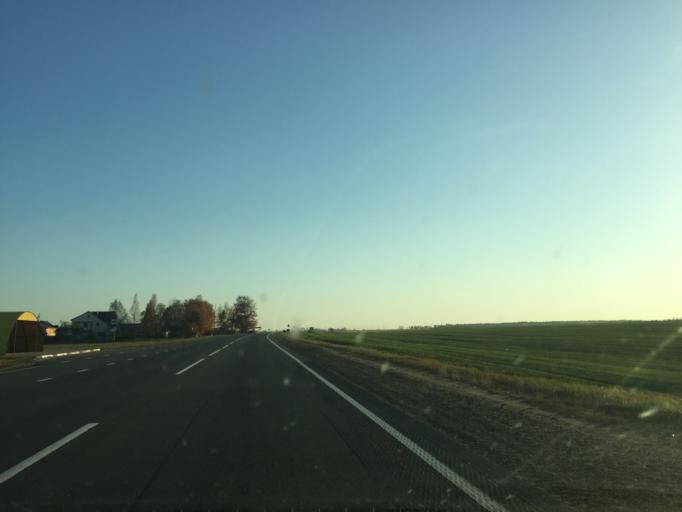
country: BY
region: Mogilev
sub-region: Mahilyowski Rayon
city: Kadino
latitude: 53.8815
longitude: 30.4883
